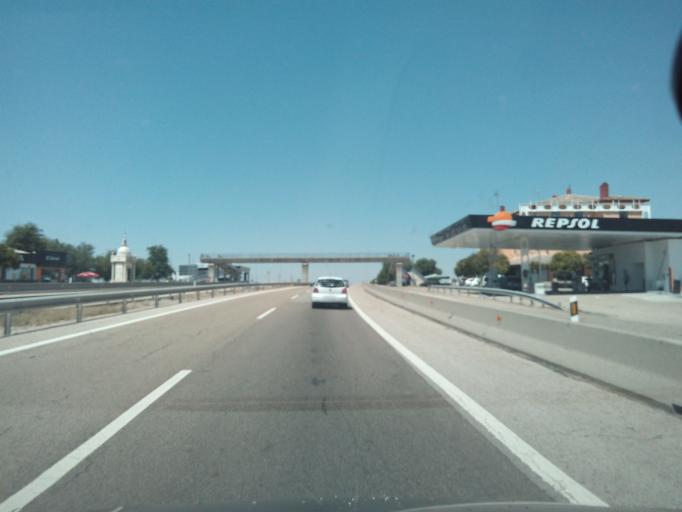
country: ES
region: Castille-La Mancha
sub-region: Province of Toledo
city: Dosbarrios
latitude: 39.8683
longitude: -3.4774
